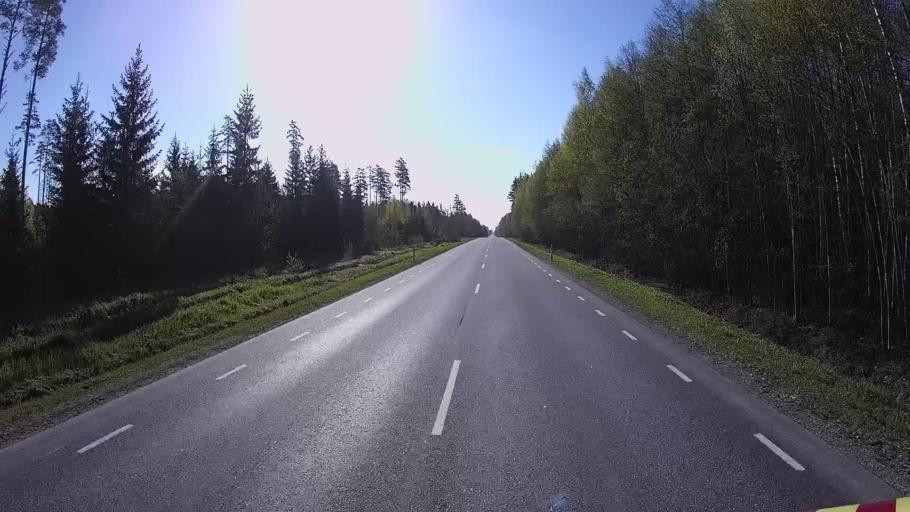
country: EE
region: Paernumaa
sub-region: Vaendra vald (alev)
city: Vandra
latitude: 58.8169
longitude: 25.1640
